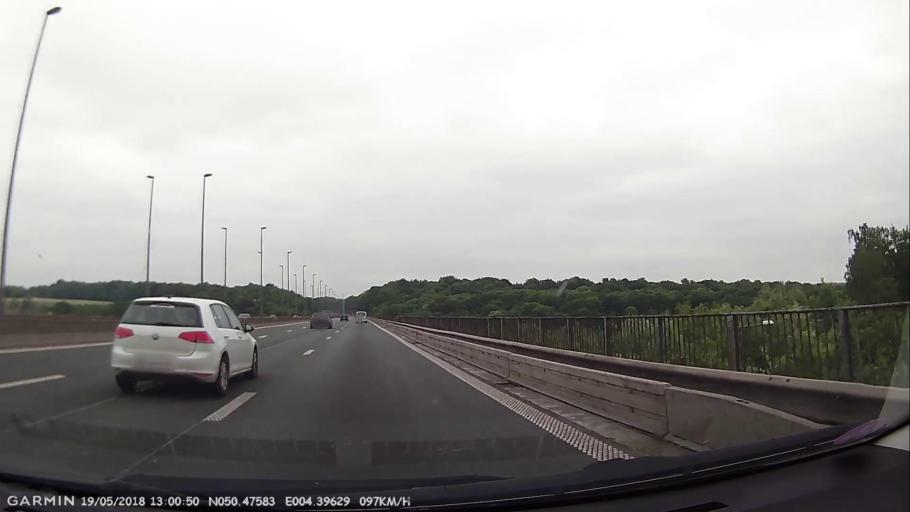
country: BE
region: Wallonia
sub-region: Province du Hainaut
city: Courcelles
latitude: 50.4758
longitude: 4.3967
